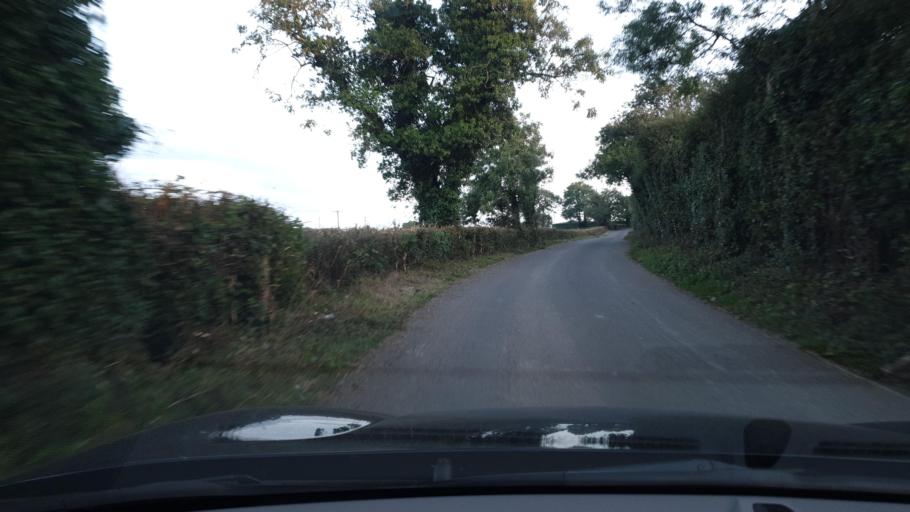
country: IE
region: Leinster
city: Balrothery
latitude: 53.5745
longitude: -6.2441
